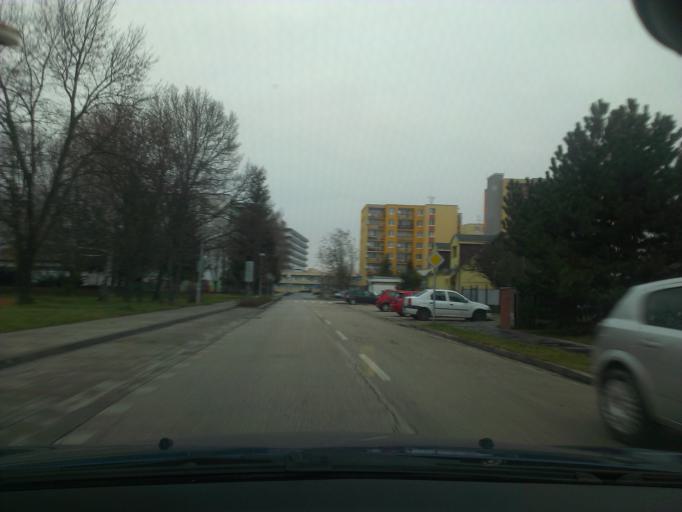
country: SK
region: Trnavsky
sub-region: Okres Trnava
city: Piestany
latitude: 48.5851
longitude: 17.8211
